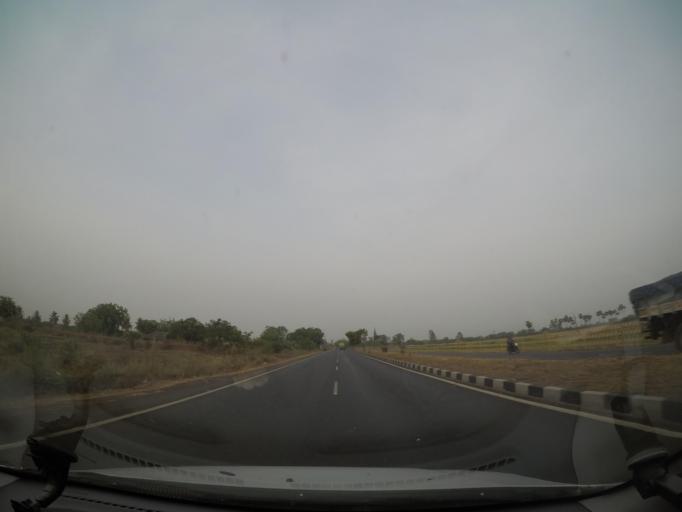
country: IN
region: Andhra Pradesh
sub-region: Krishna
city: Gannavaram
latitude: 16.6180
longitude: 80.9273
